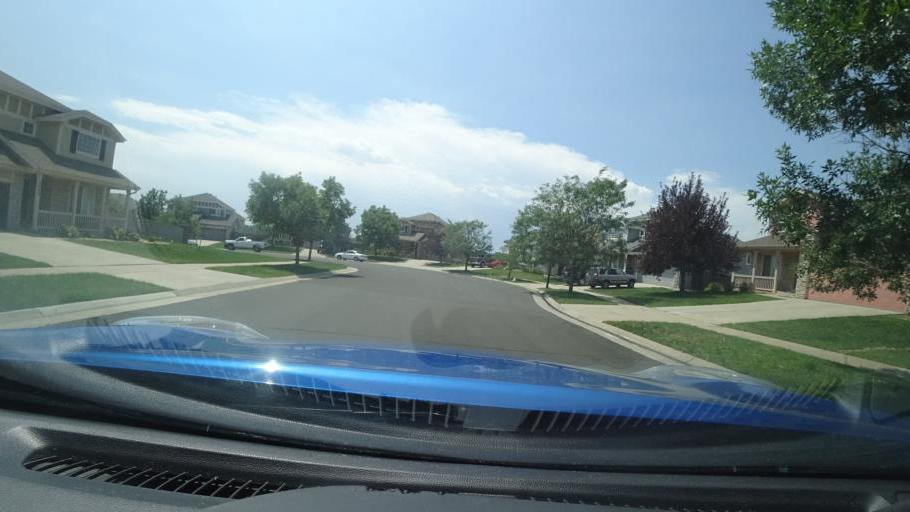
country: US
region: Colorado
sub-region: Adams County
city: Aurora
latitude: 39.6710
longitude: -104.7662
